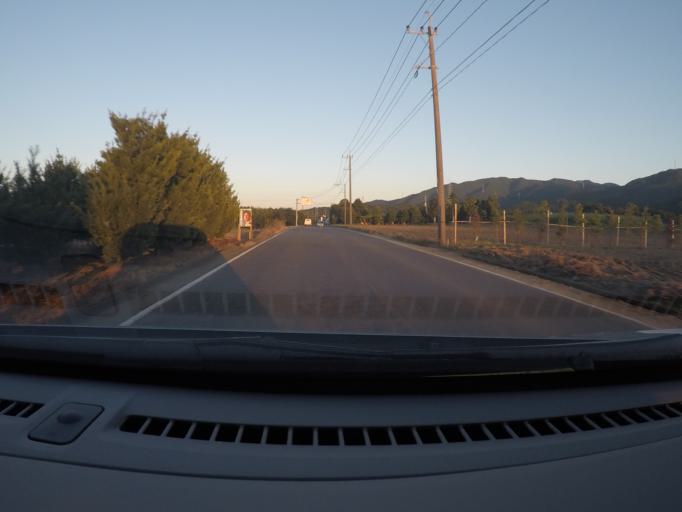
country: JP
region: Kagoshima
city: Izumi
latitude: 32.0532
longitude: 130.3295
